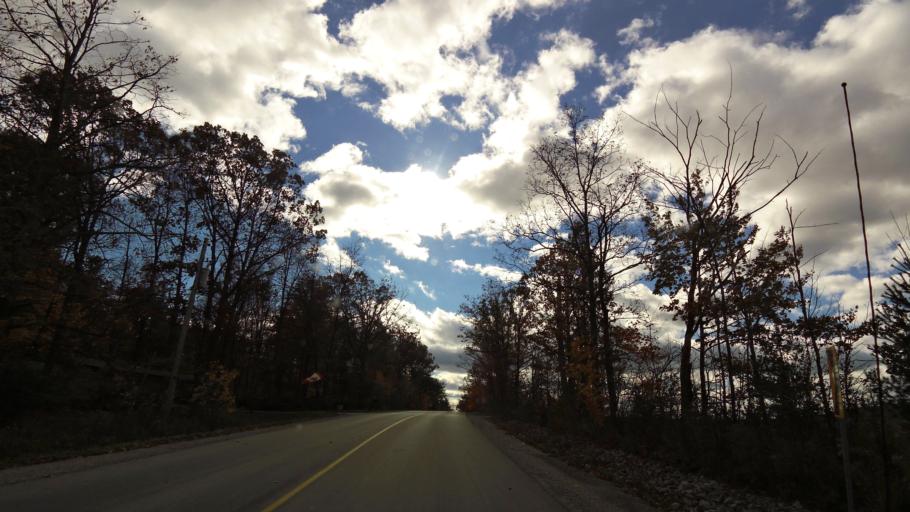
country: CA
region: Ontario
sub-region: Halton
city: Milton
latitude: 43.4740
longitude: -79.8004
